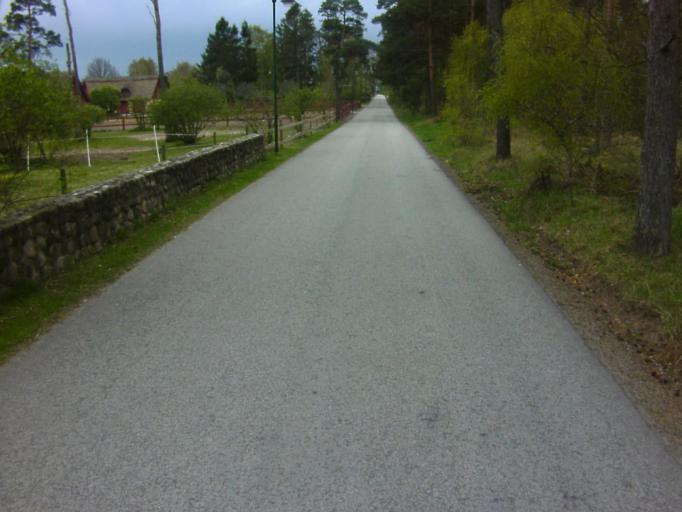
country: SE
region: Skane
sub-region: Kavlinge Kommun
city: Loddekopinge
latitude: 55.7525
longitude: 12.9916
